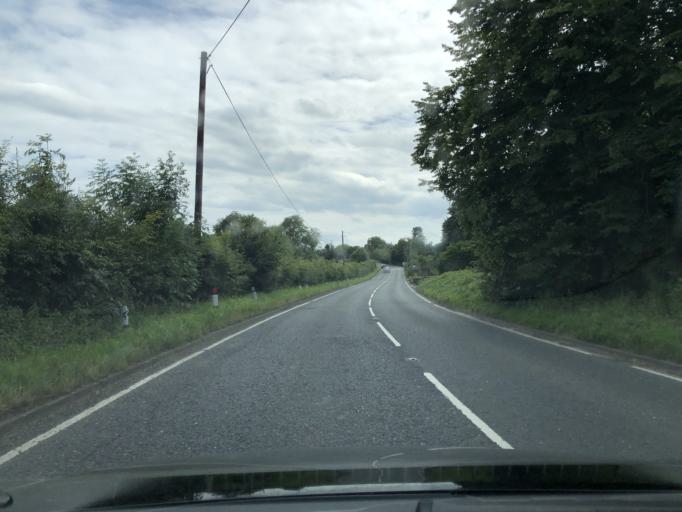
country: GB
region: Northern Ireland
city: Ballynahinch
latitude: 54.3609
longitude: -5.8574
